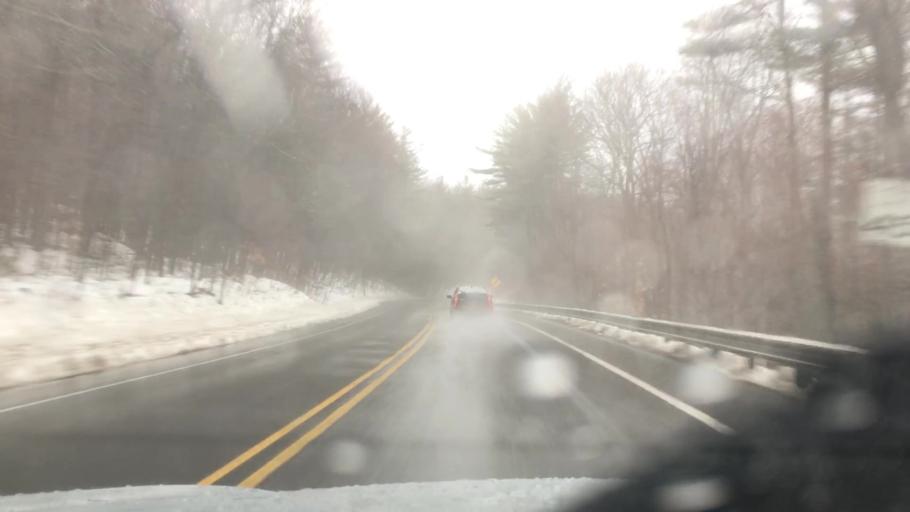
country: US
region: Massachusetts
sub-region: Franklin County
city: Wendell
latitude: 42.5150
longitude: -72.3287
